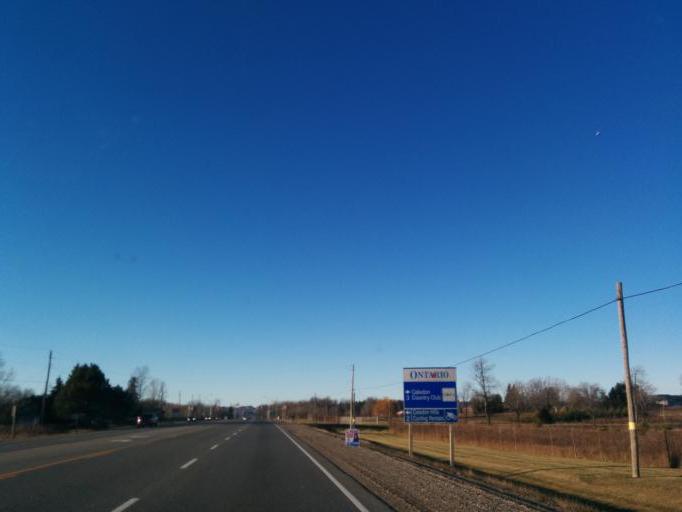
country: CA
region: Ontario
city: Brampton
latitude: 43.7989
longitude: -79.9128
